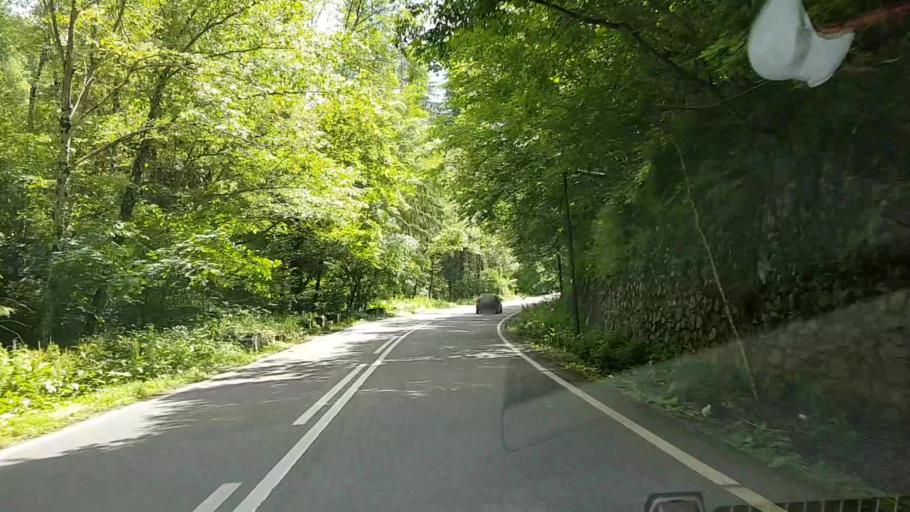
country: RO
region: Suceava
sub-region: Comuna Crucea
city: Crucea
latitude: 47.3072
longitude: 25.6260
